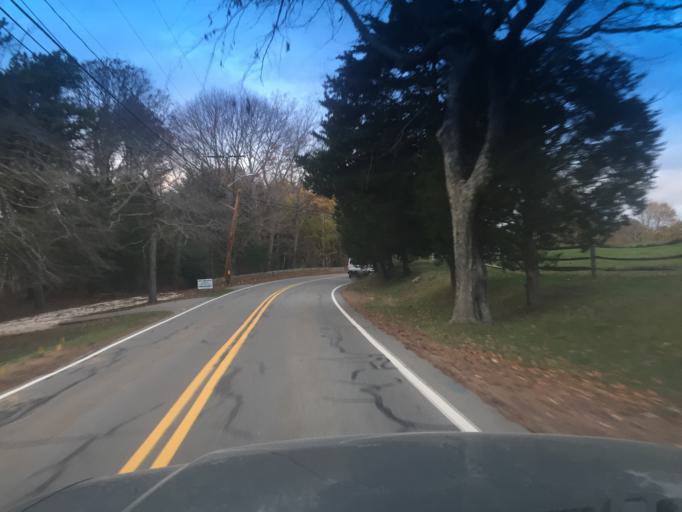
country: US
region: Massachusetts
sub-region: Barnstable County
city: Pocasset
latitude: 41.6726
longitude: -70.6092
